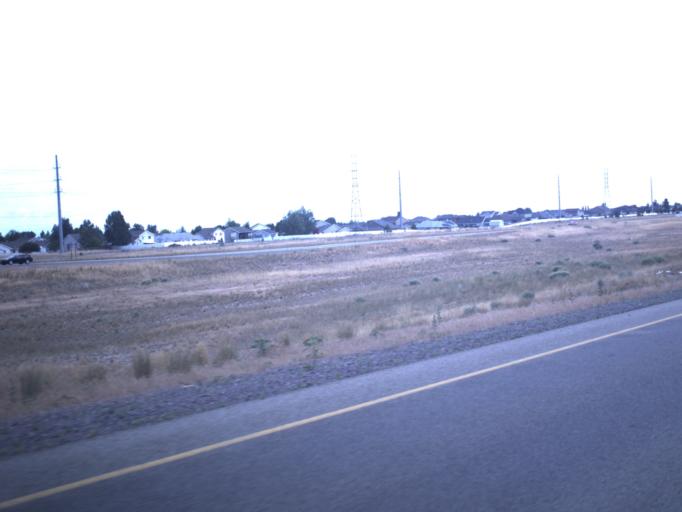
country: US
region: Utah
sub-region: Salt Lake County
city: Herriman
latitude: 40.5343
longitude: -112.0136
